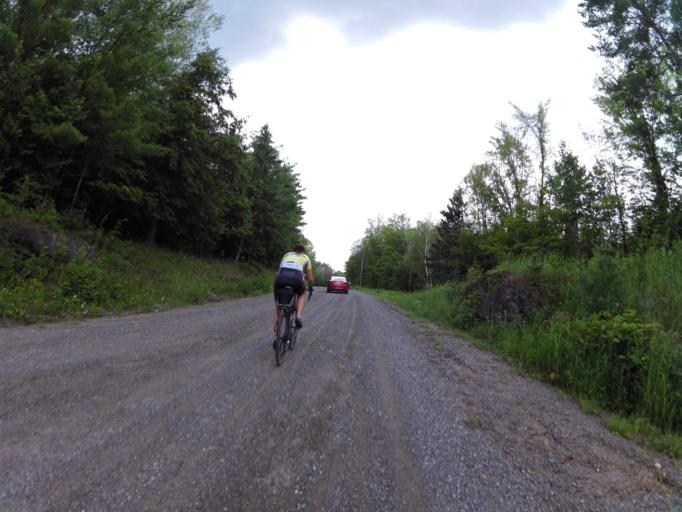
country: CA
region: Ontario
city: Renfrew
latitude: 45.1216
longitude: -76.6254
